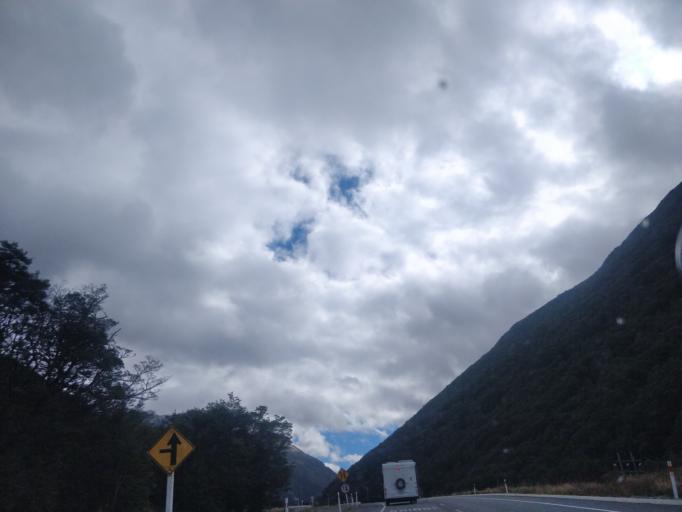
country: NZ
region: West Coast
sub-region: Grey District
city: Greymouth
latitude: -42.9493
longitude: 171.5683
